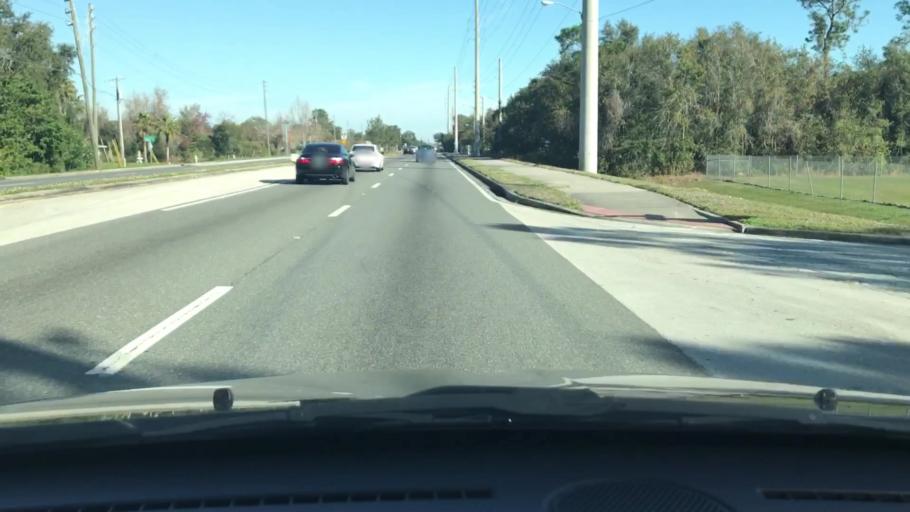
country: US
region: Florida
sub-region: Osceola County
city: Campbell
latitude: 28.2509
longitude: -81.4362
